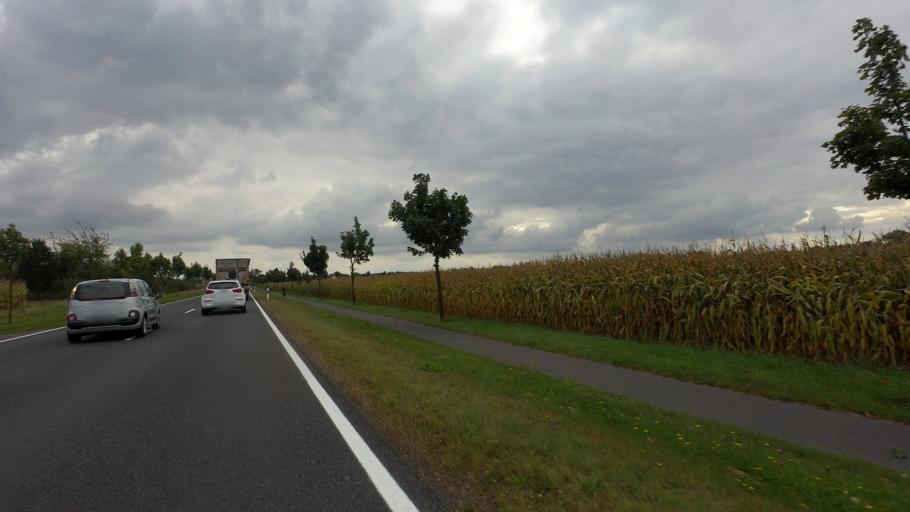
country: DE
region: Saxony
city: Neschwitz
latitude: 51.2793
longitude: 14.3367
